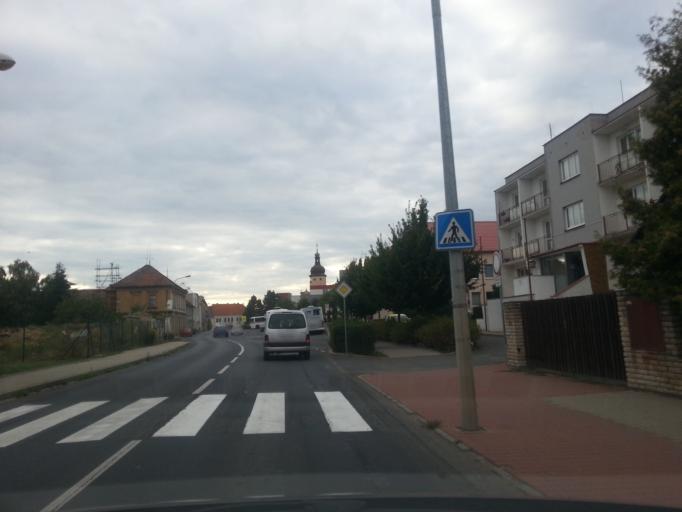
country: CZ
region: Central Bohemia
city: Unhost'
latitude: 50.0856
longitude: 14.1356
